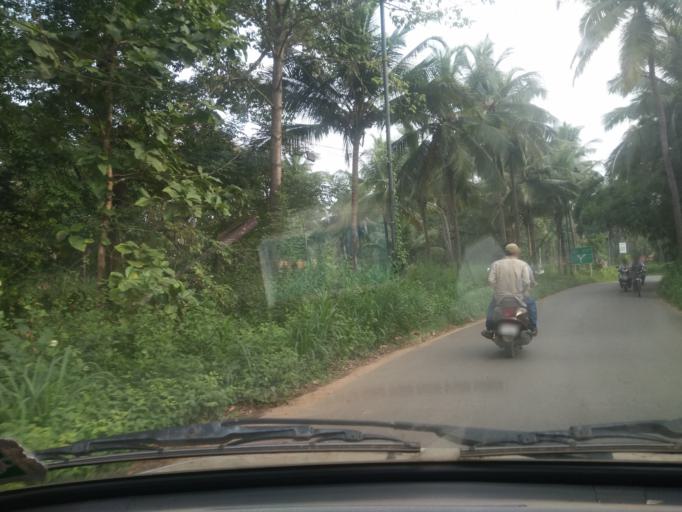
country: IN
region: Goa
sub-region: South Goa
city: Varca
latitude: 15.2254
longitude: 73.9447
